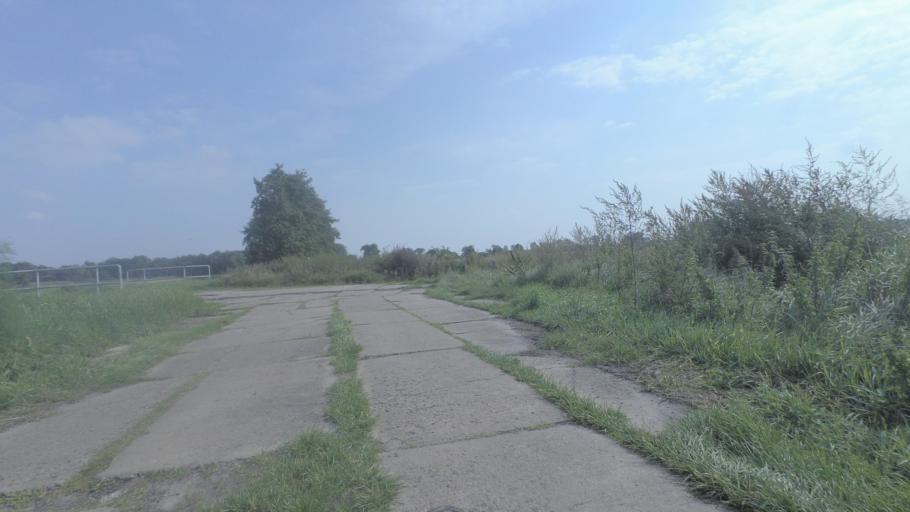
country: DE
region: Brandenburg
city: Rangsdorf
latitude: 52.2648
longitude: 13.4314
